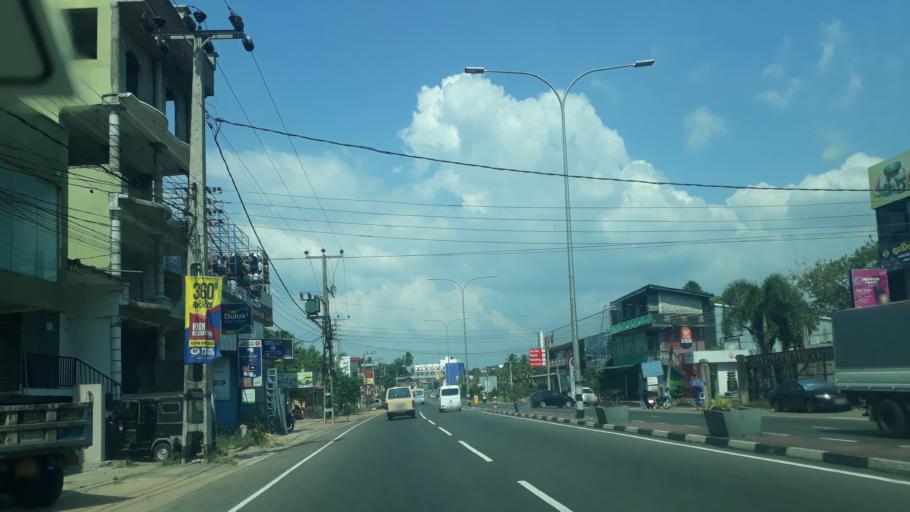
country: LK
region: Western
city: Gampaha
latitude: 7.0747
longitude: 80.0177
